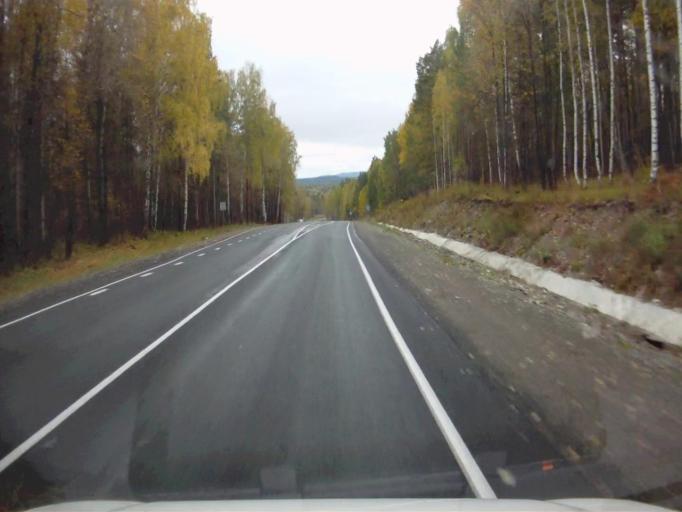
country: RU
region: Chelyabinsk
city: Nyazepetrovsk
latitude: 56.0518
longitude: 59.7430
